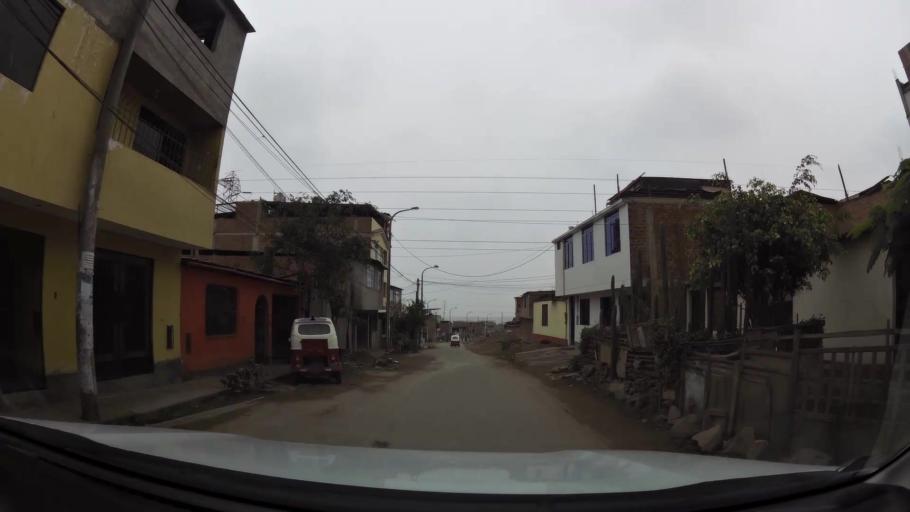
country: PE
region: Lima
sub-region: Lima
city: Surco
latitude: -12.2171
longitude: -76.9178
